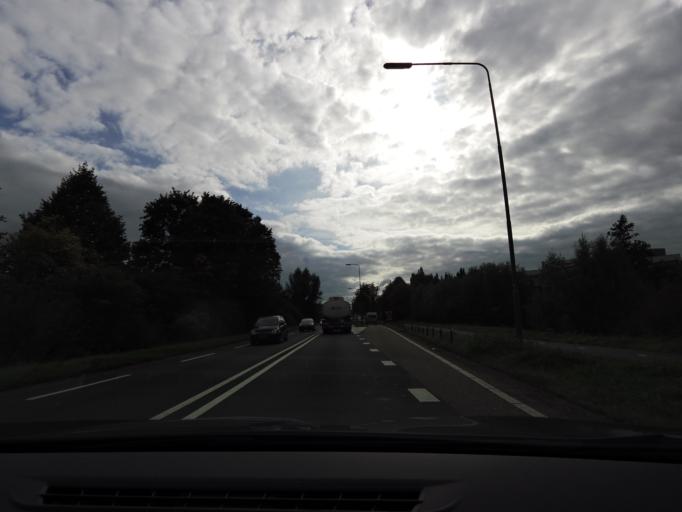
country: NL
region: Utrecht
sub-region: Gemeente Nieuwegein
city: Nieuwegein
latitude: 52.0389
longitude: 5.1045
